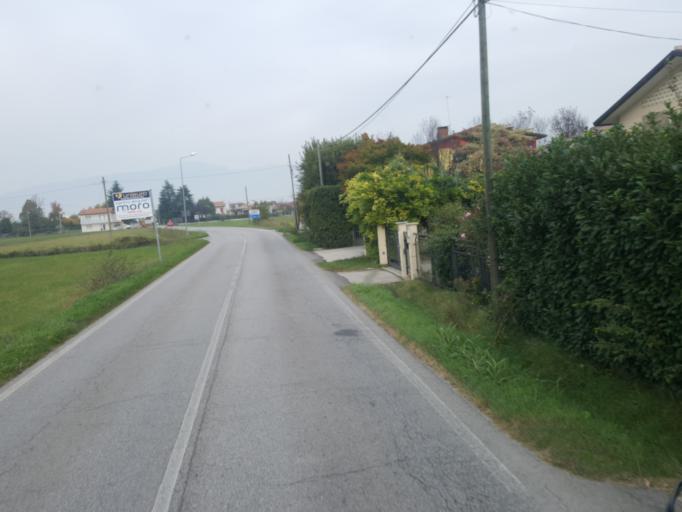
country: IT
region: Veneto
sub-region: Provincia di Treviso
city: Castello di Godego
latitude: 45.6991
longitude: 11.8753
